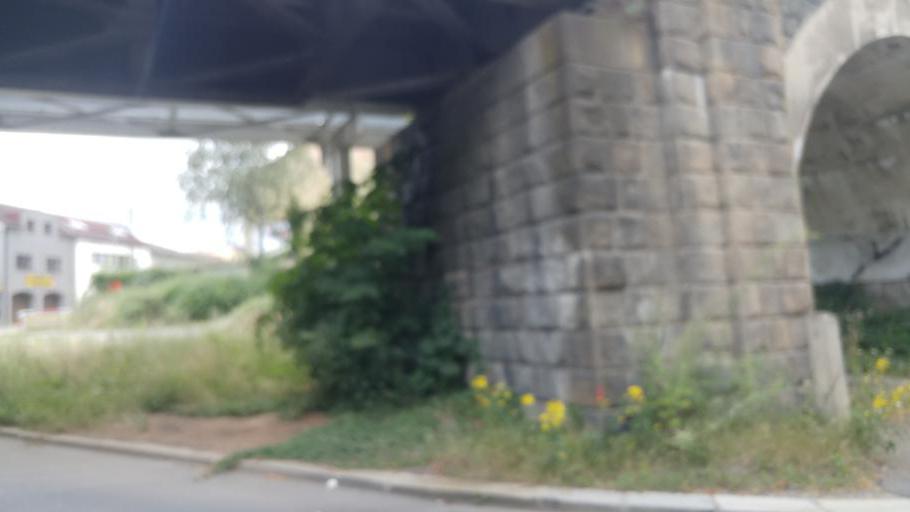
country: CZ
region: Praha
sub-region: Praha 9
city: Vysocany
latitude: 50.0877
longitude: 14.5159
